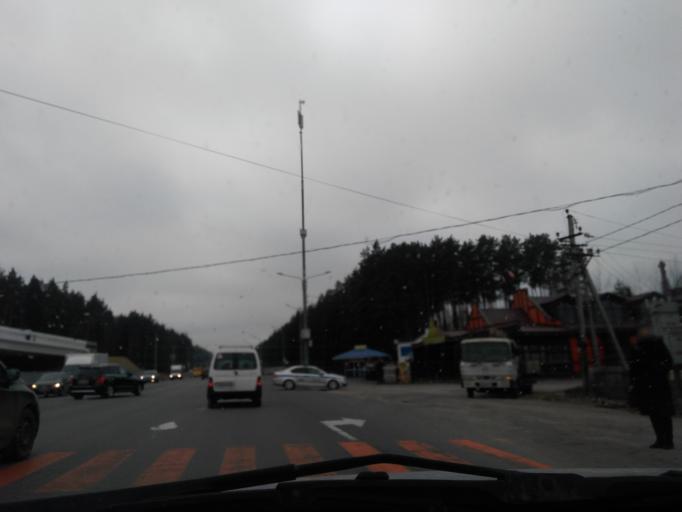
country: RU
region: Moskovskaya
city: Vatutinki
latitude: 55.4867
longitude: 37.3235
